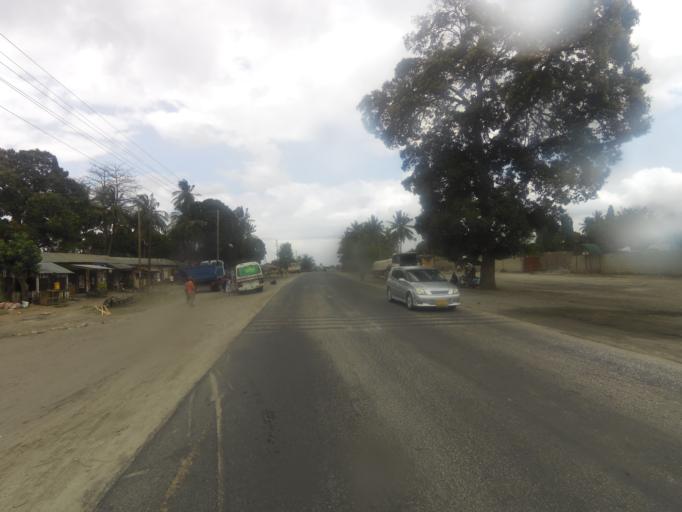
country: TZ
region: Pwani
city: Vikindu
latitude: -6.9779
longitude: 39.2895
